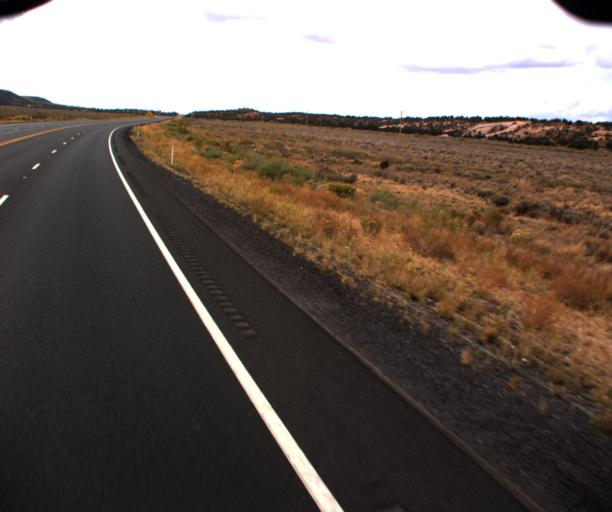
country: US
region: Arizona
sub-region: Navajo County
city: Kayenta
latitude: 36.5709
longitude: -110.4807
